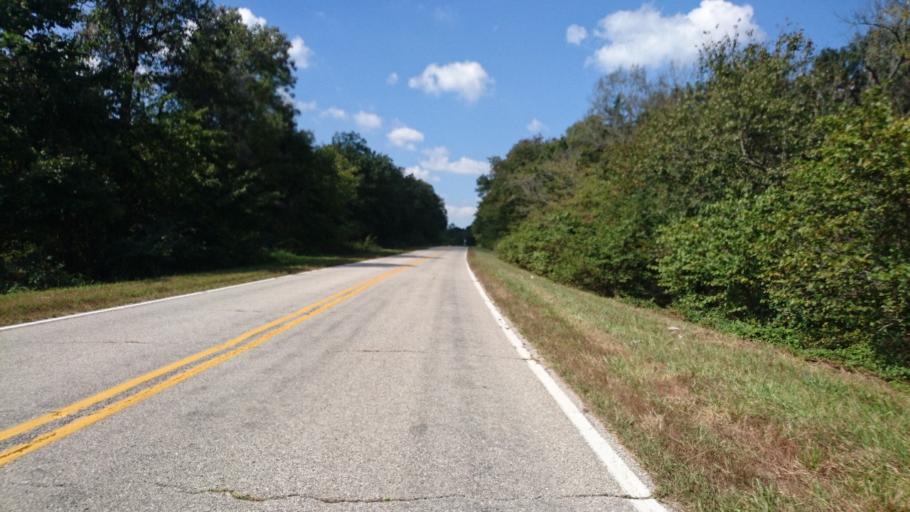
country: US
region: Missouri
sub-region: Pulaski County
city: Richland
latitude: 37.7523
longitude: -92.4939
